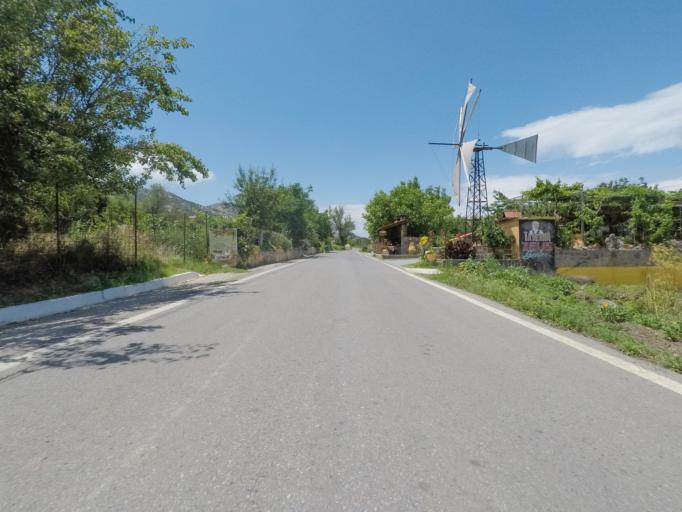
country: GR
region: Crete
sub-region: Nomos Irakleiou
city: Mokhos
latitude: 35.1687
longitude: 25.4462
